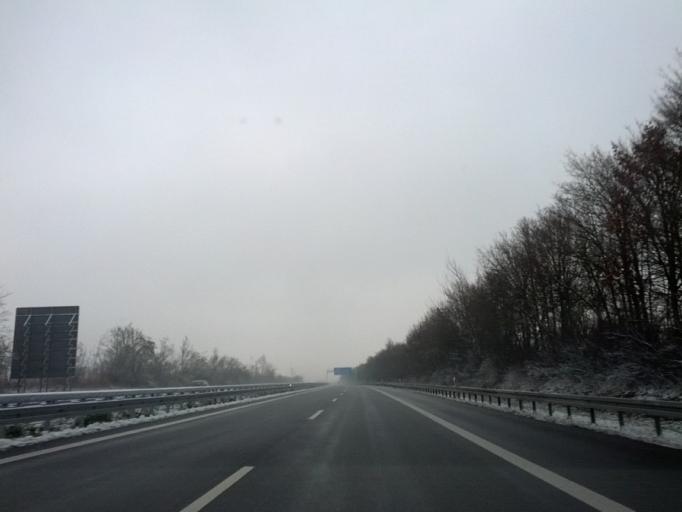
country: DE
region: Bavaria
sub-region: Regierungsbezirk Unterfranken
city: Biebelried
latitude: 49.7655
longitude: 10.1027
